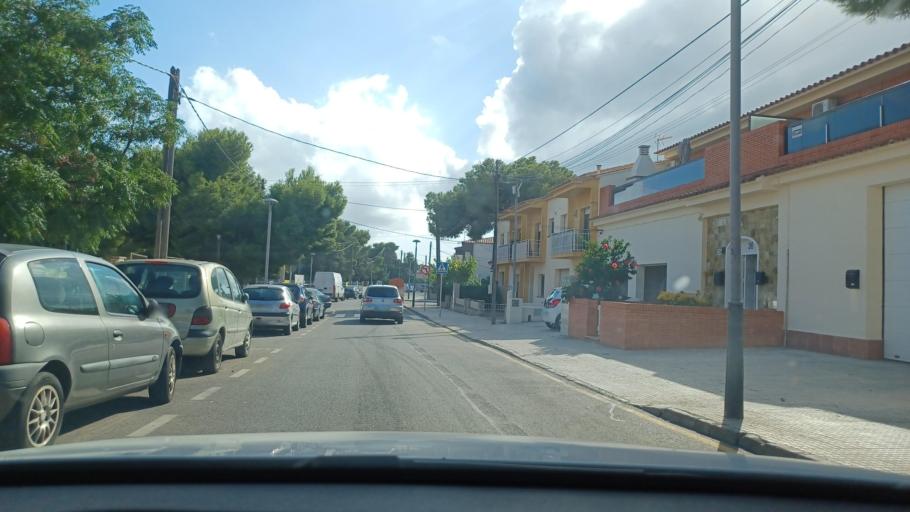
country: ES
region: Catalonia
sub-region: Provincia de Tarragona
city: Colldejou
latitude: 41.0025
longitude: 0.9314
